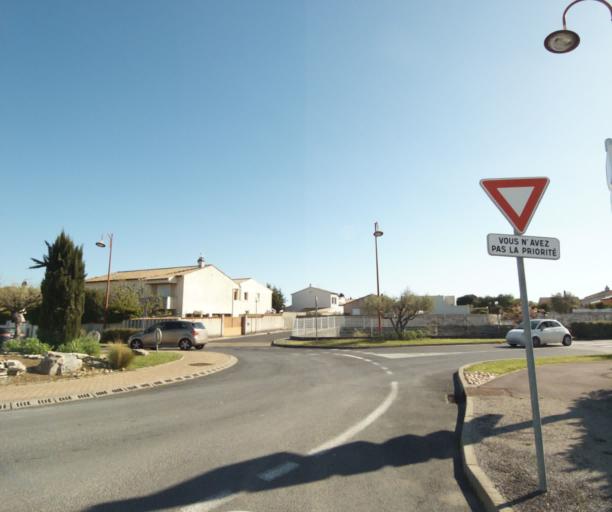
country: FR
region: Languedoc-Roussillon
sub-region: Departement de l'Herault
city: Perols
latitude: 43.5700
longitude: 3.9437
